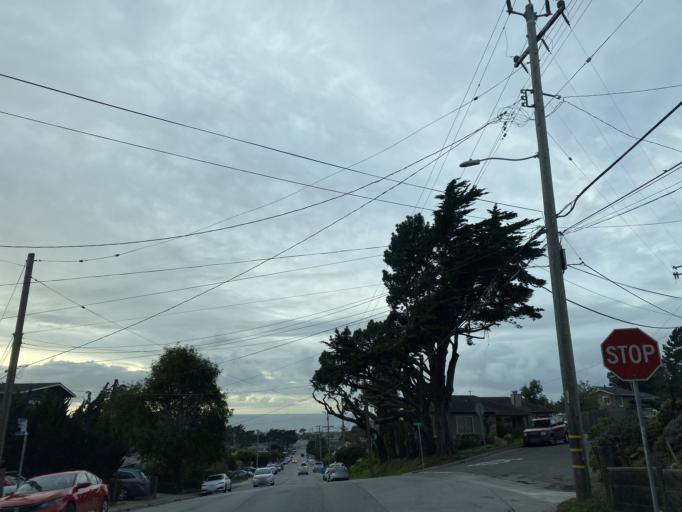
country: US
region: California
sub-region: San Mateo County
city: Colma
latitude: 37.6511
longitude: -122.4833
